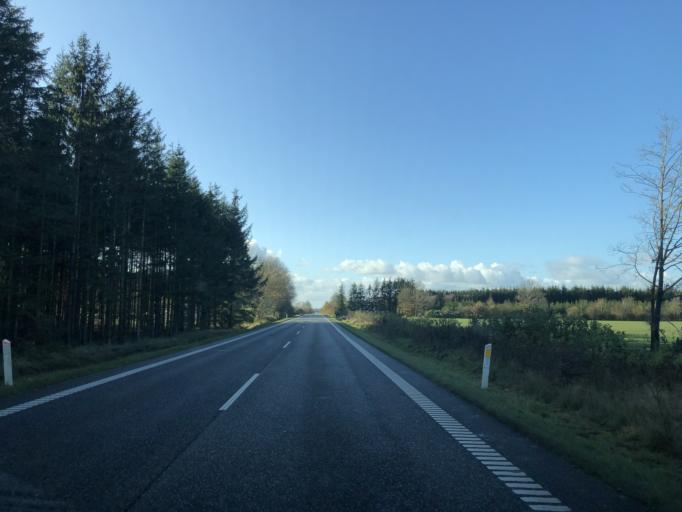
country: DK
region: Central Jutland
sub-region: Ikast-Brande Kommune
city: Bording Kirkeby
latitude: 56.1375
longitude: 9.3730
